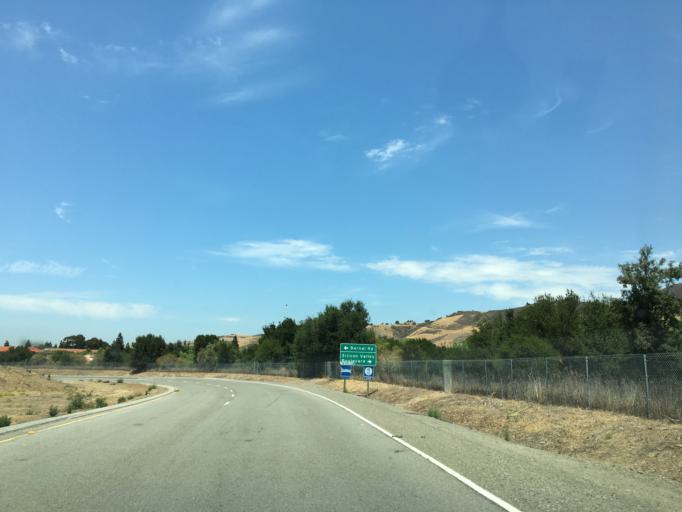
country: US
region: California
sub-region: Santa Clara County
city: Seven Trees
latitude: 37.2440
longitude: -121.7710
